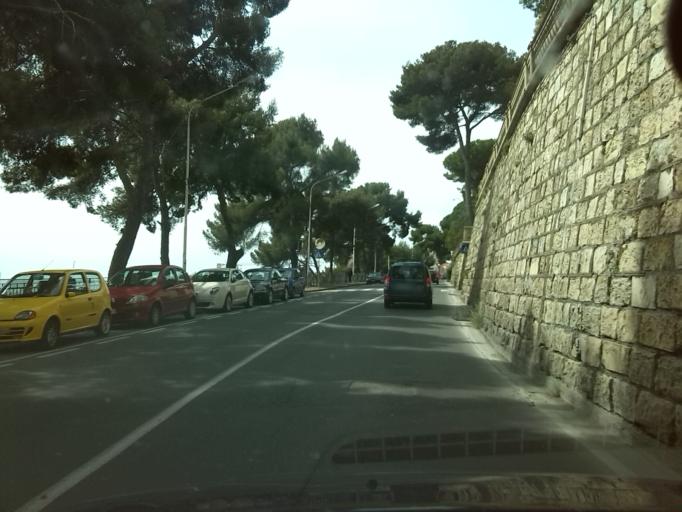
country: IT
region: Liguria
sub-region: Provincia di Imperia
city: Imperia
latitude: 43.8843
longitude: 8.0263
